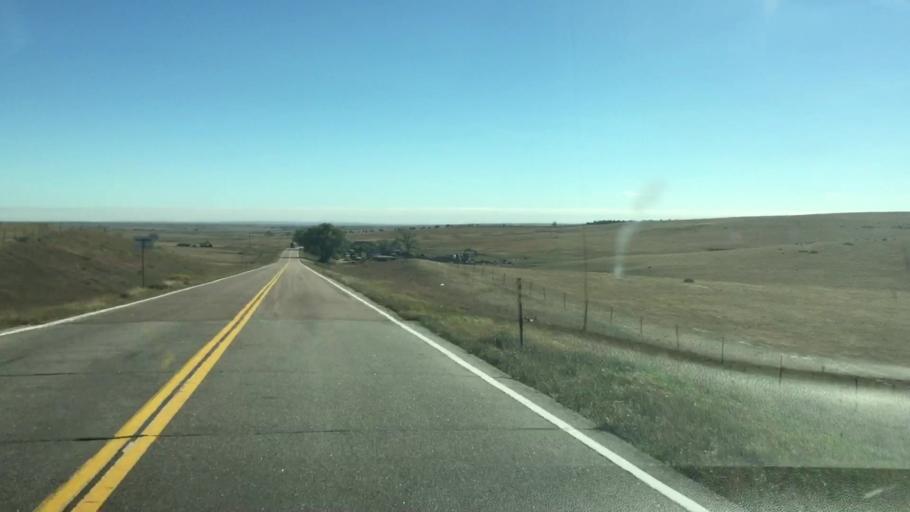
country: US
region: Colorado
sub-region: Lincoln County
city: Limon
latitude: 39.2881
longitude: -103.9660
